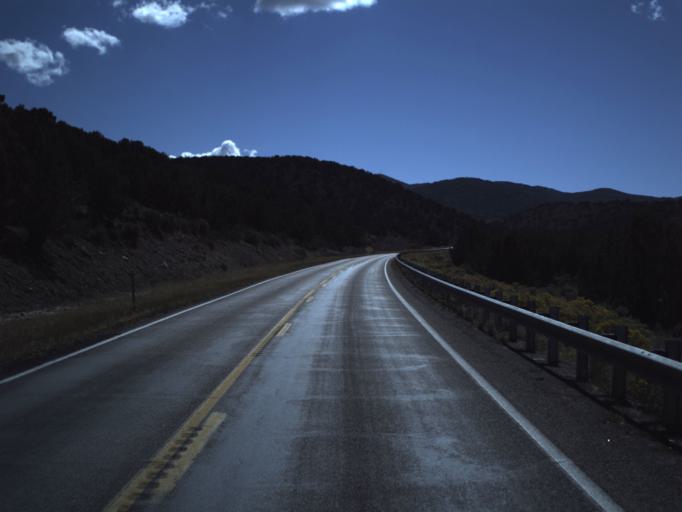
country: US
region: Utah
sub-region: Washington County
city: Enterprise
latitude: 37.5525
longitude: -113.6874
